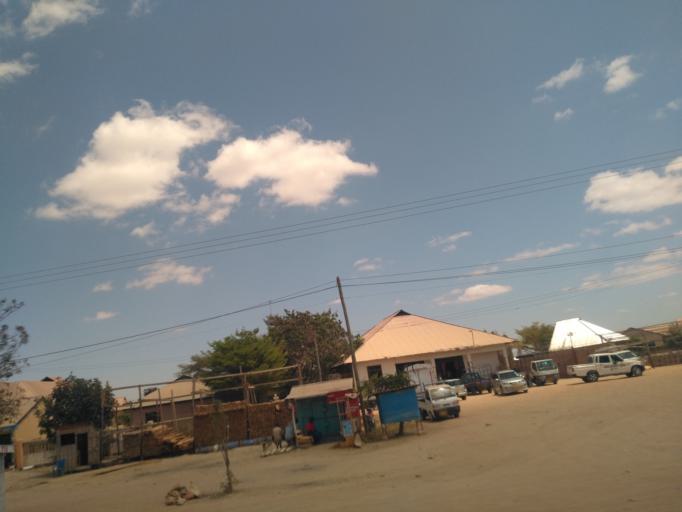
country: TZ
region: Dodoma
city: Kisasa
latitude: -6.1640
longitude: 35.7879
